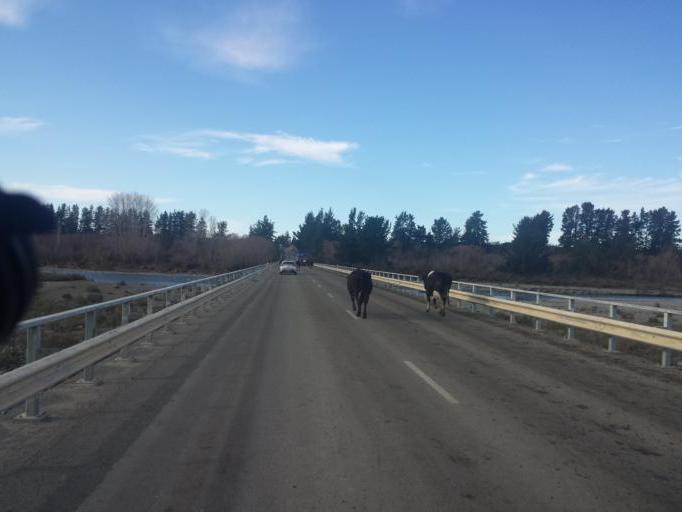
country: NZ
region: Canterbury
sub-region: Timaru District
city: Pleasant Point
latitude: -43.9741
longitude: 171.3012
